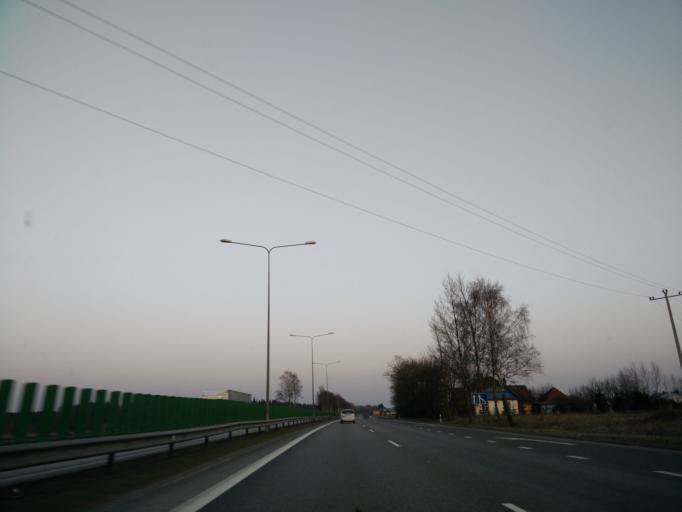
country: LT
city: Lentvaris
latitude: 54.7072
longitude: 24.9978
